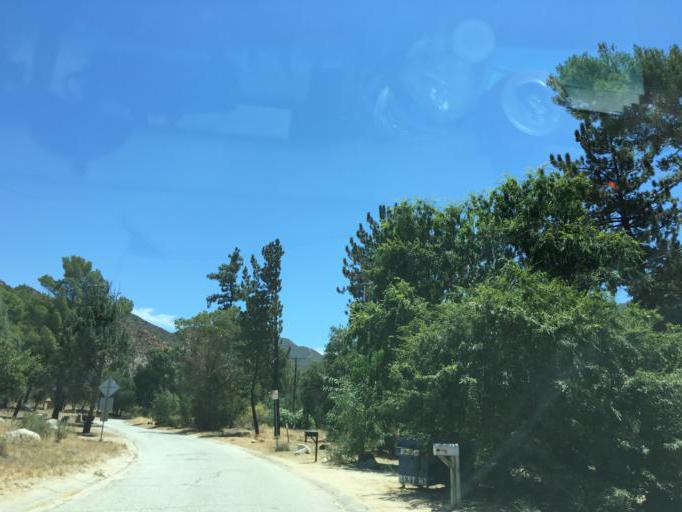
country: US
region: California
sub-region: Los Angeles County
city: La Crescenta-Montrose
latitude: 34.2863
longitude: -118.2273
